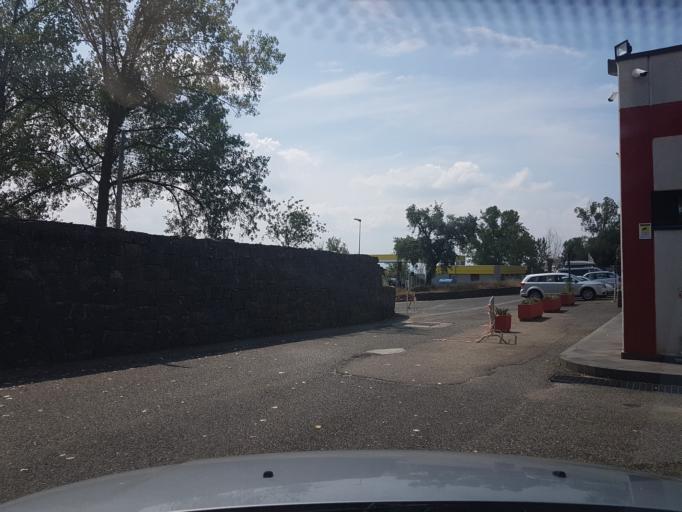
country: IT
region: Sardinia
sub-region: Provincia di Oristano
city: Abbasanta
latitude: 40.1103
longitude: 8.7921
